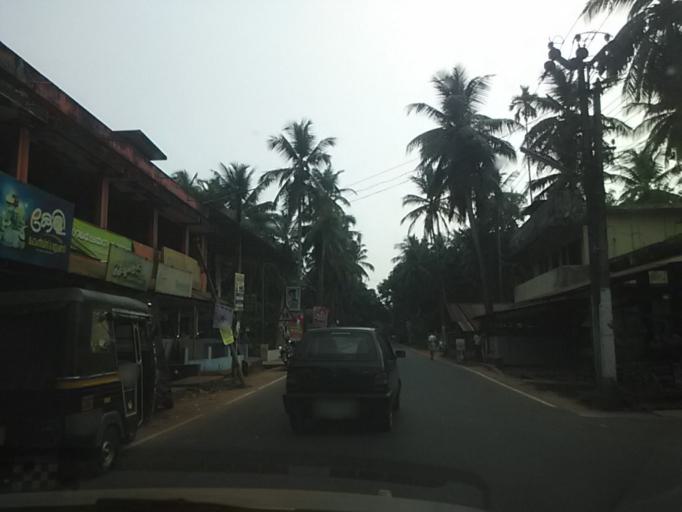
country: IN
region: Kerala
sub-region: Kozhikode
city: Naduvannur
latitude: 11.5037
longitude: 75.7734
